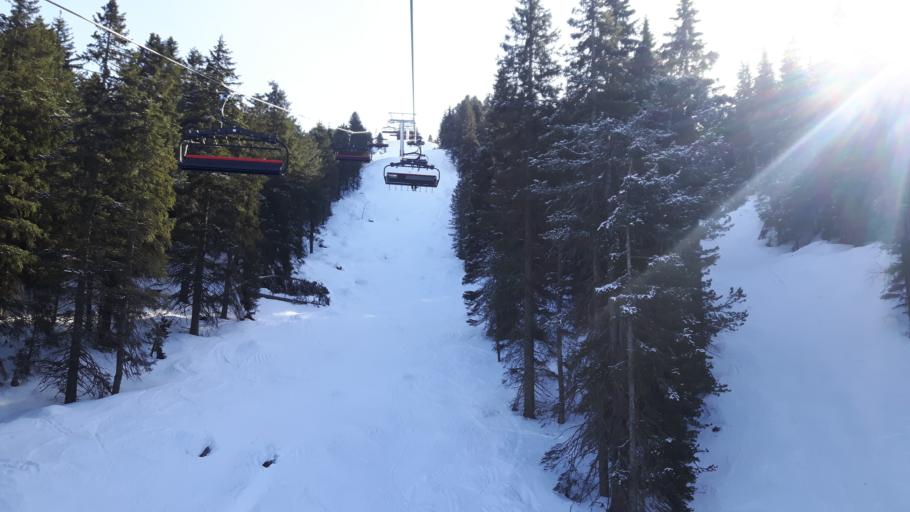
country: IT
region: Trentino-Alto Adige
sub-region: Provincia di Trento
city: Tesero
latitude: 46.3564
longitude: 11.5347
